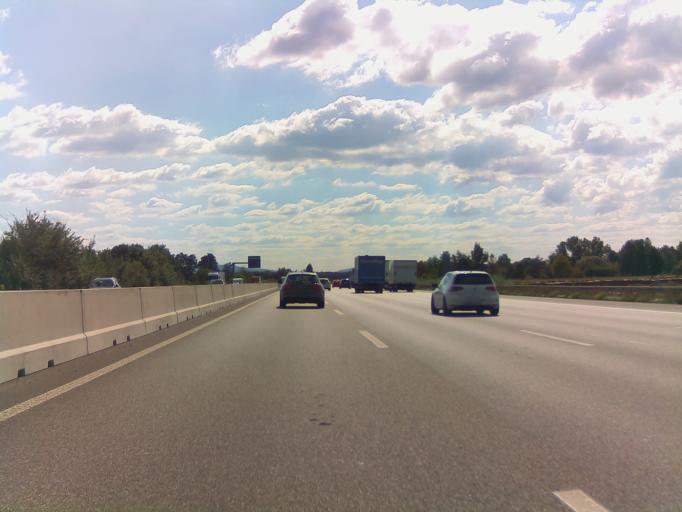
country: DE
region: Hesse
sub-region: Regierungsbezirk Darmstadt
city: Erzhausen
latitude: 49.9381
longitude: 8.6121
